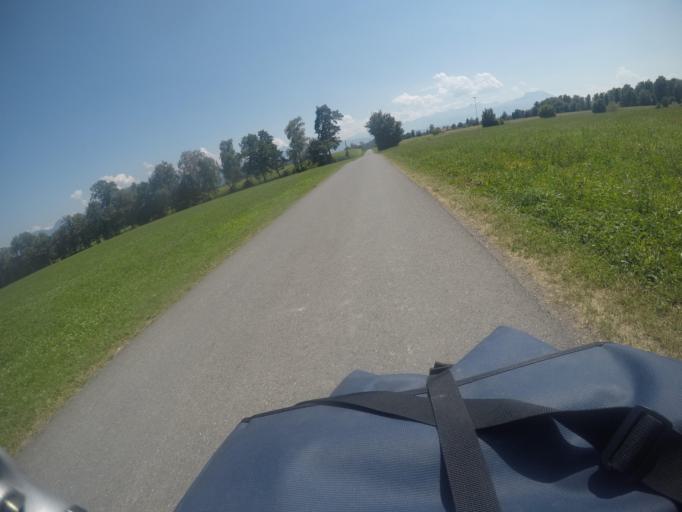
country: CH
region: Saint Gallen
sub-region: Wahlkreis Rheintal
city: Altstatten
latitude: 47.3612
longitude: 9.5694
